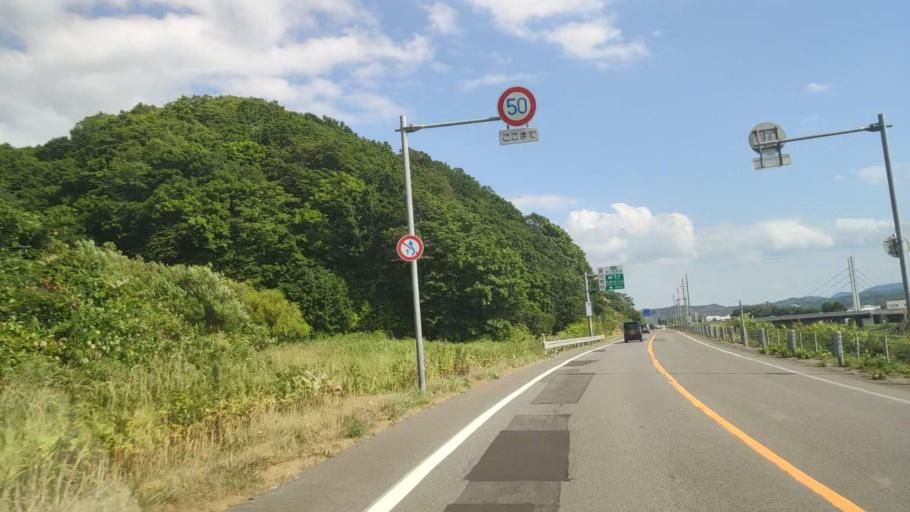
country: JP
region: Hokkaido
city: Rumoi
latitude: 43.9501
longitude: 141.6477
